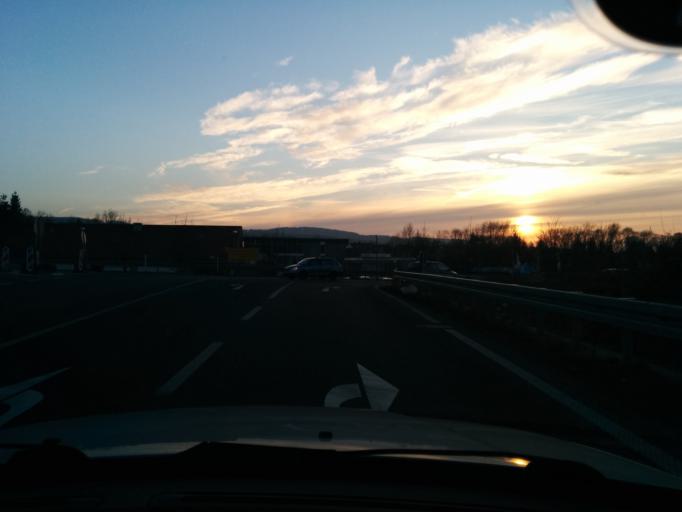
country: DE
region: Hesse
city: Hessisch Lichtenau
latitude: 51.2077
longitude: 9.7129
